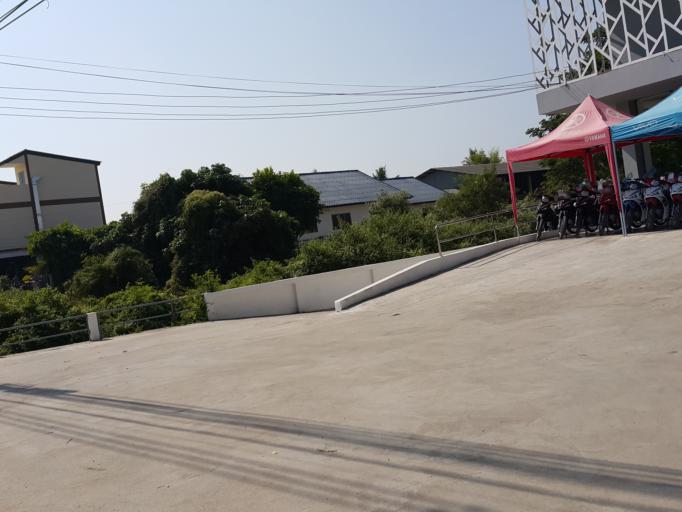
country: TH
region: Lamphun
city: Pa Sang
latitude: 18.5379
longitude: 98.9390
